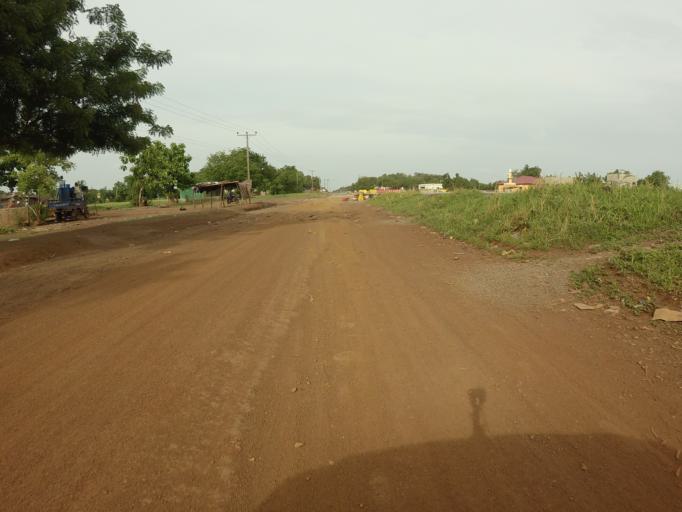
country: GH
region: Northern
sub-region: Yendi
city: Yendi
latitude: 9.9270
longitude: -0.2107
